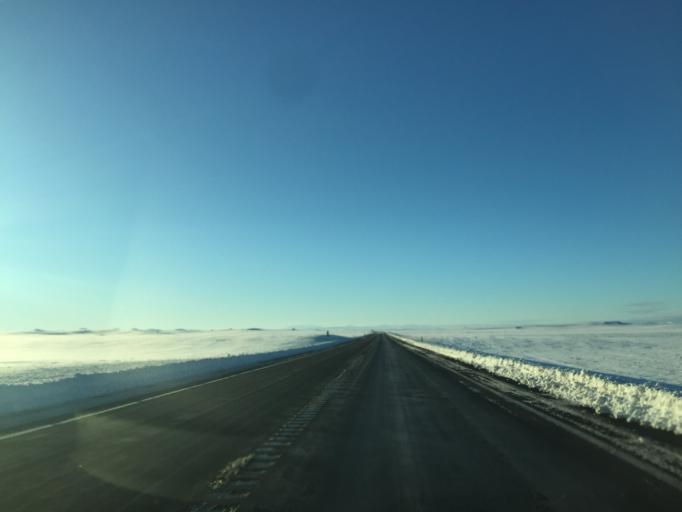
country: US
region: Washington
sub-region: Grant County
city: Soap Lake
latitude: 47.6199
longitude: -119.4338
